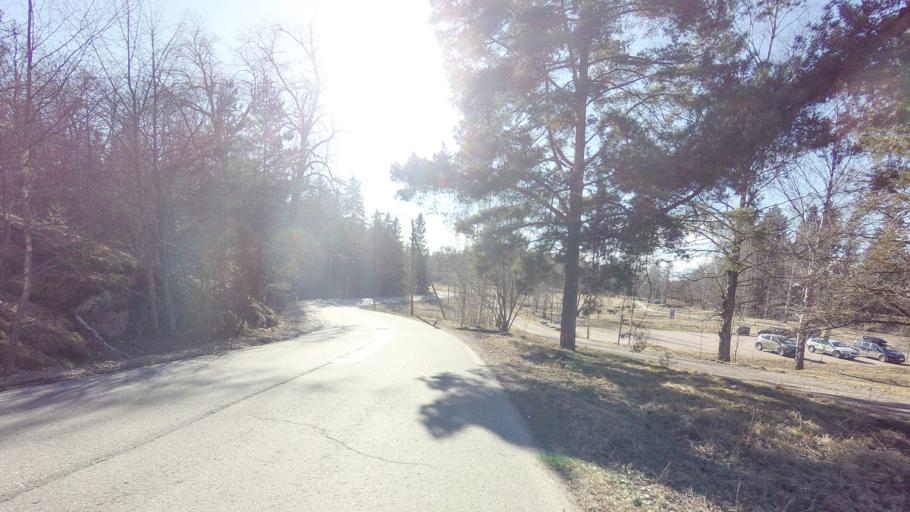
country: FI
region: Uusimaa
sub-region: Helsinki
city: Helsinki
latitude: 60.1774
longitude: 25.0338
